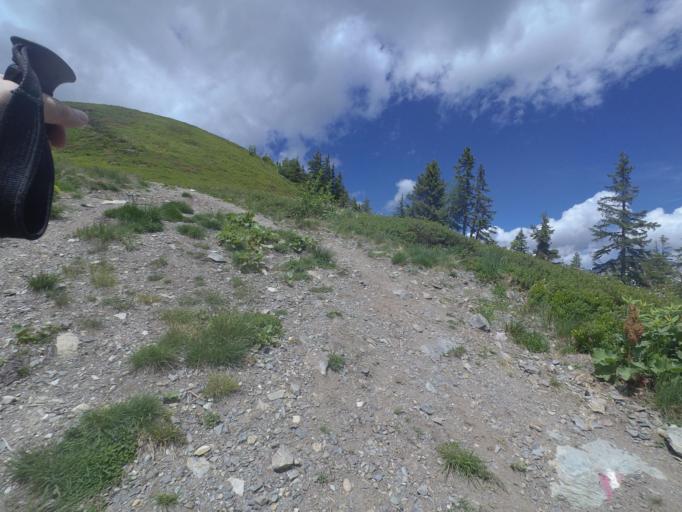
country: AT
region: Salzburg
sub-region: Politischer Bezirk Zell am See
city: Viehhofen
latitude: 47.4033
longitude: 12.6959
